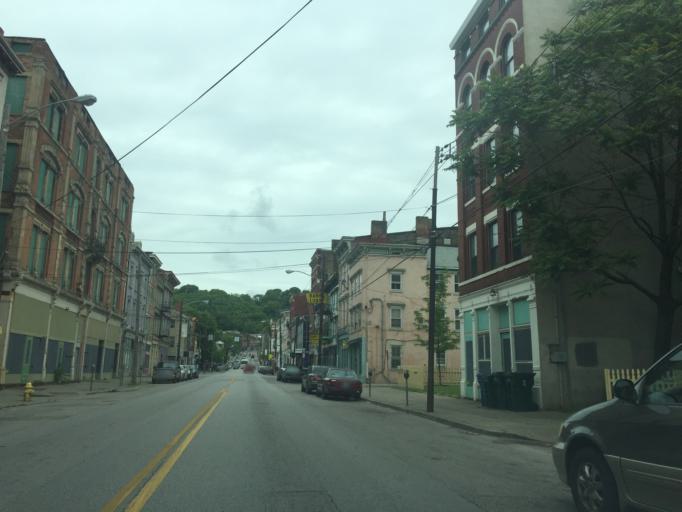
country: US
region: Kentucky
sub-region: Campbell County
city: Newport
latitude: 39.1148
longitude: -84.5164
